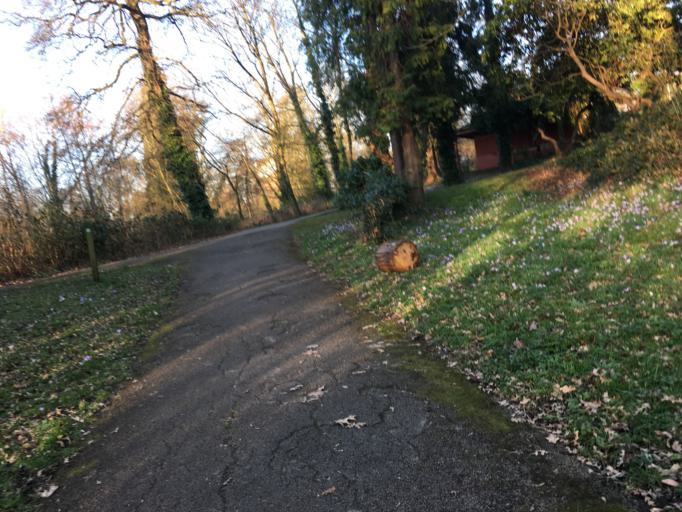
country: GB
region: England
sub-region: Greater London
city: Hendon
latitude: 51.5843
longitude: -0.2114
